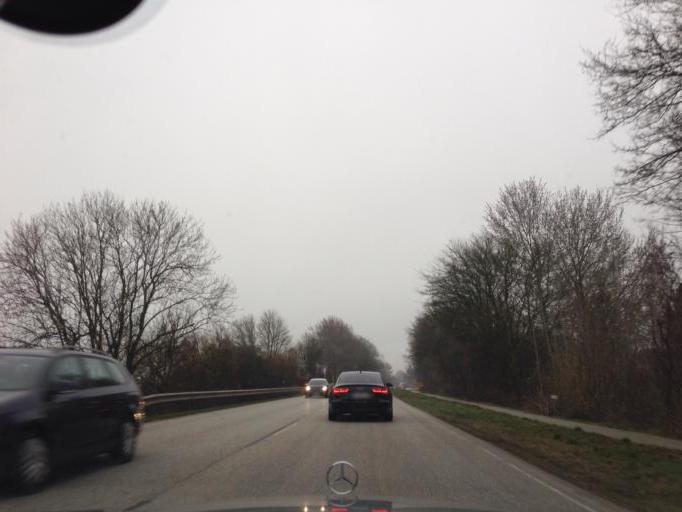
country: DE
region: Schleswig-Holstein
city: Kirchbarkau
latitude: 54.2122
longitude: 10.1490
